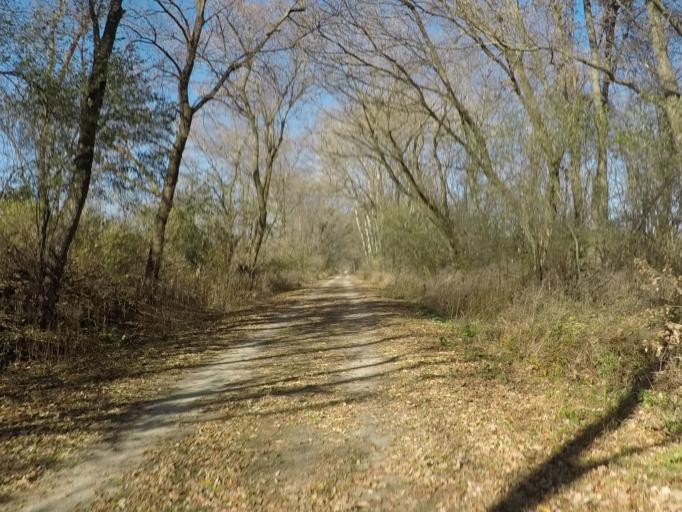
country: US
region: Wisconsin
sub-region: Dane County
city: Deerfield
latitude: 43.0476
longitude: -89.0575
